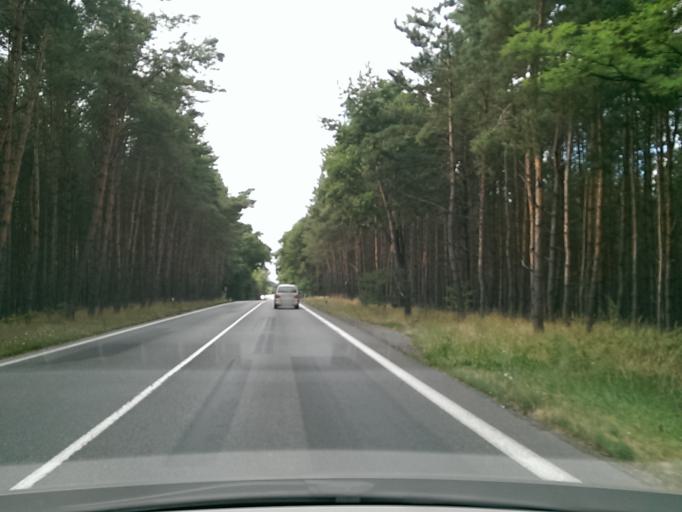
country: CZ
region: Central Bohemia
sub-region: Okres Nymburk
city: Podebrady
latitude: 50.1108
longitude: 15.1336
